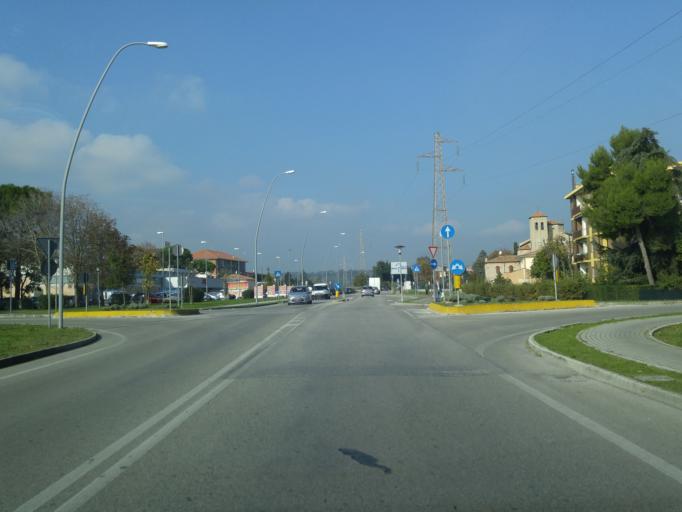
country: IT
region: The Marches
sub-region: Provincia di Pesaro e Urbino
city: Fano
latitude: 43.8355
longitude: 13.0090
